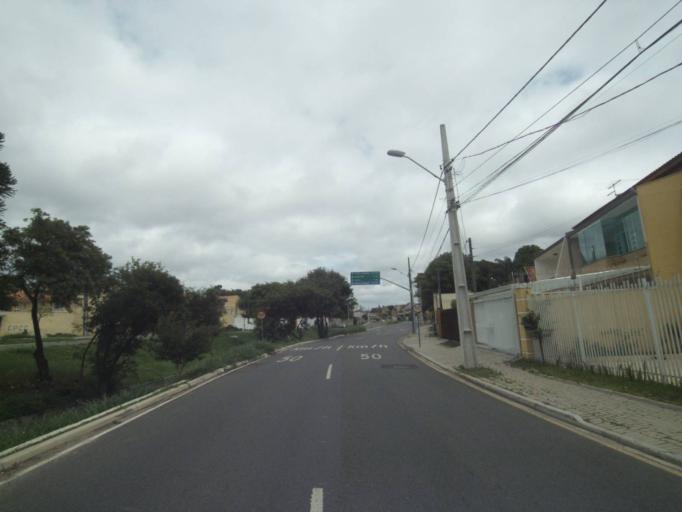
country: BR
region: Parana
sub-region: Pinhais
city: Pinhais
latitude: -25.4346
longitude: -49.2223
